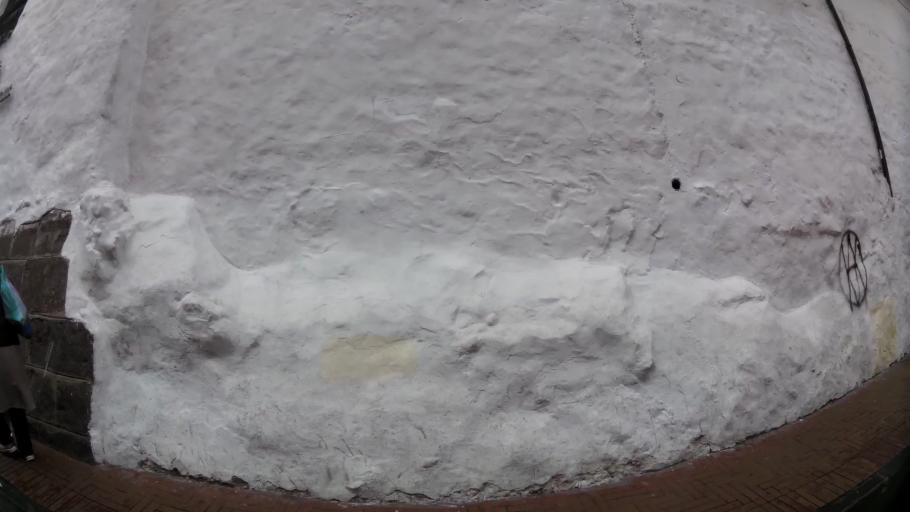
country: EC
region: Pichincha
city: Quito
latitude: -0.2175
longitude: -78.5093
